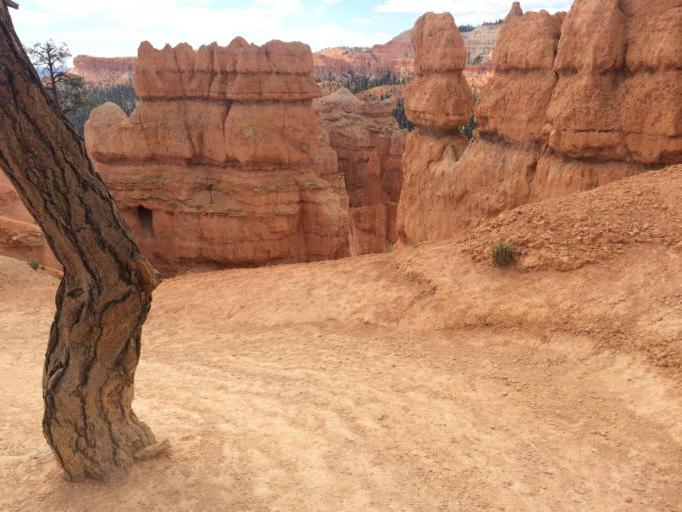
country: US
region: Utah
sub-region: Garfield County
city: Panguitch
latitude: 37.6273
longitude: -112.1600
